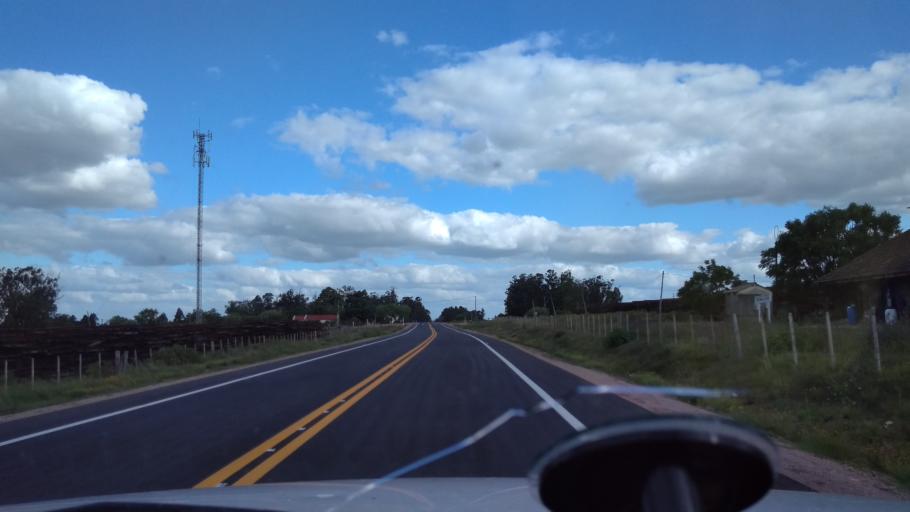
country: UY
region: Florida
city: Casupa
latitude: -33.9983
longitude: -55.6506
